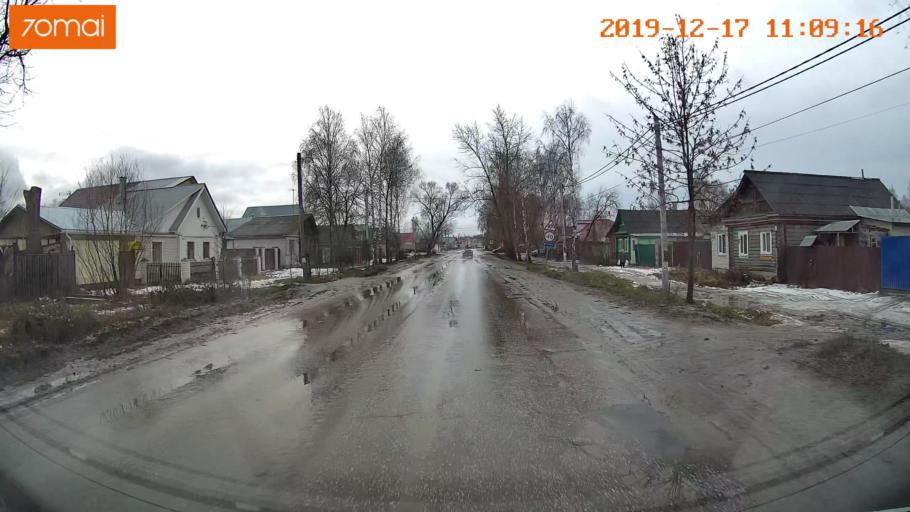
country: RU
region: Vladimir
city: Gus'-Khrustal'nyy
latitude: 55.6019
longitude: 40.6426
